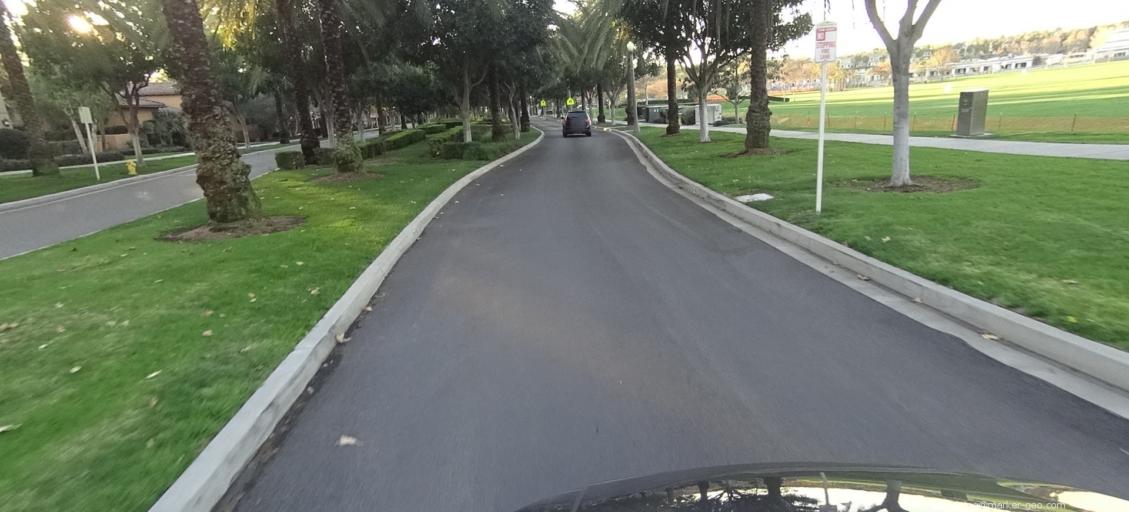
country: US
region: California
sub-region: Orange County
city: Ladera Ranch
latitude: 33.5513
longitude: -117.6337
